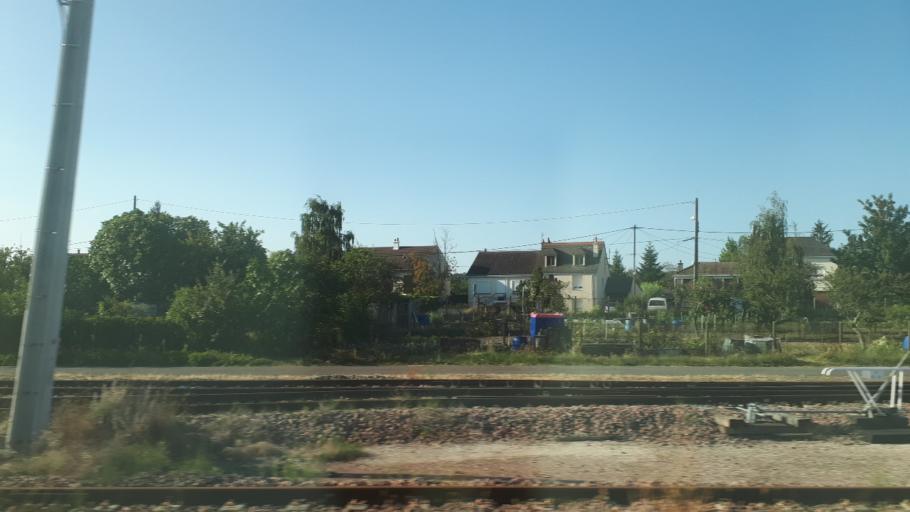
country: FR
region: Centre
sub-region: Departement d'Indre-et-Loire
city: Saint-Pierre-des-Corps
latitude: 47.3911
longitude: 0.7491
